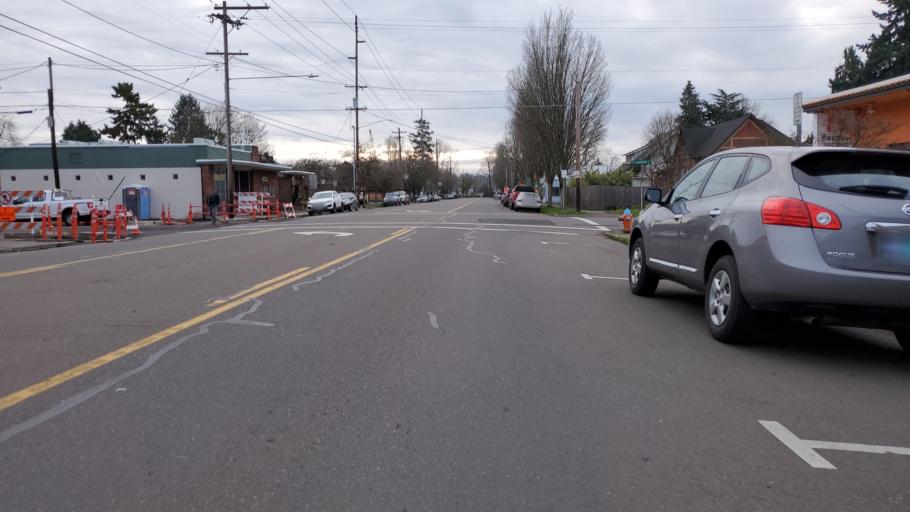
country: US
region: Oregon
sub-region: Clackamas County
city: Gladstone
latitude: 45.3799
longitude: -122.5944
